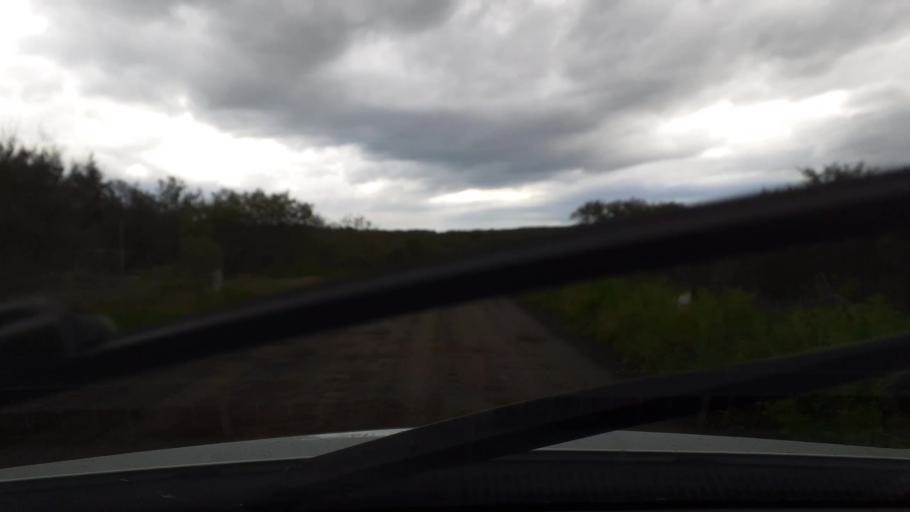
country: IS
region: West
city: Borgarnes
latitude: 64.6149
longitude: -21.9498
